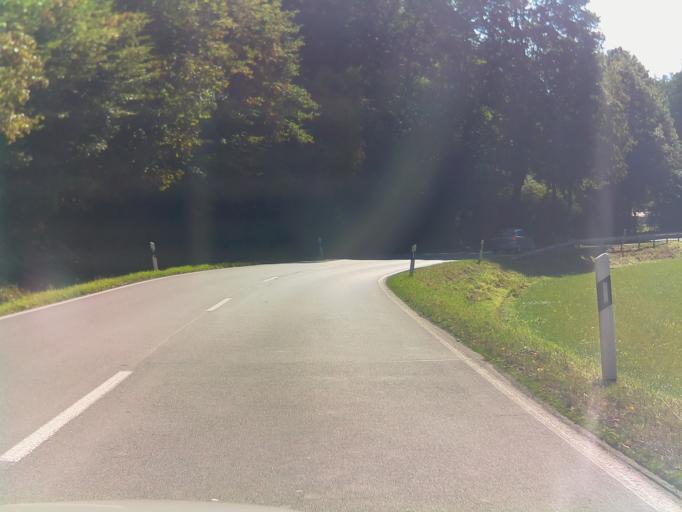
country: DE
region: Thuringia
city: Leutenberg
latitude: 50.5749
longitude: 11.4446
